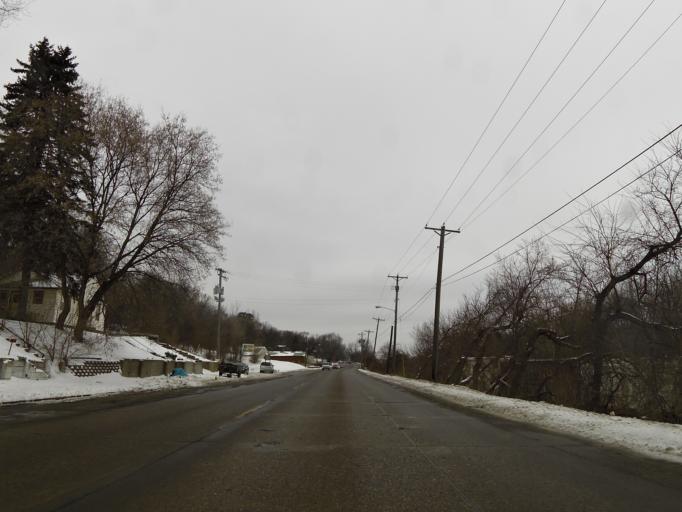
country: US
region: Minnesota
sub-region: Dakota County
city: South Saint Paul
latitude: 44.9148
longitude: -93.0552
